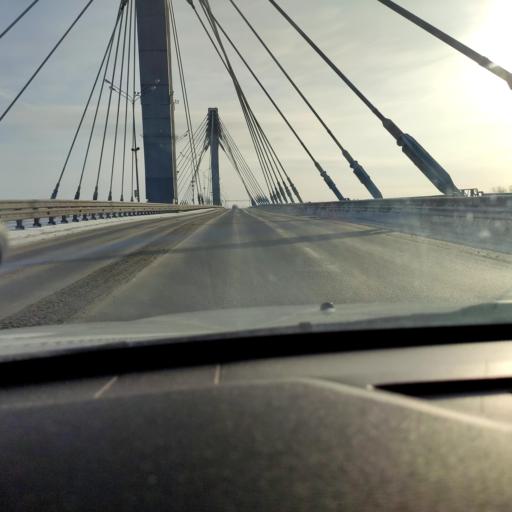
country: RU
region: Samara
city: Smyshlyayevka
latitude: 53.1817
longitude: 50.3054
